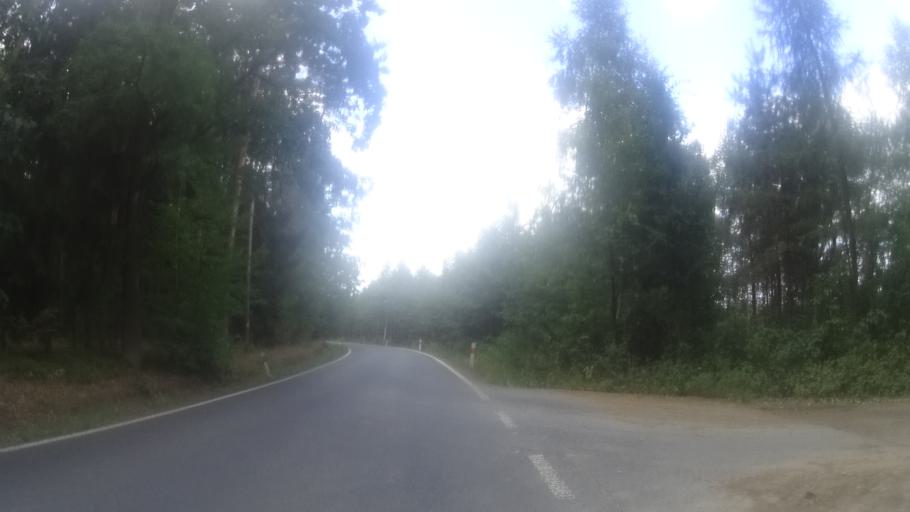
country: CZ
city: Borohradek
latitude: 50.0799
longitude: 16.1221
